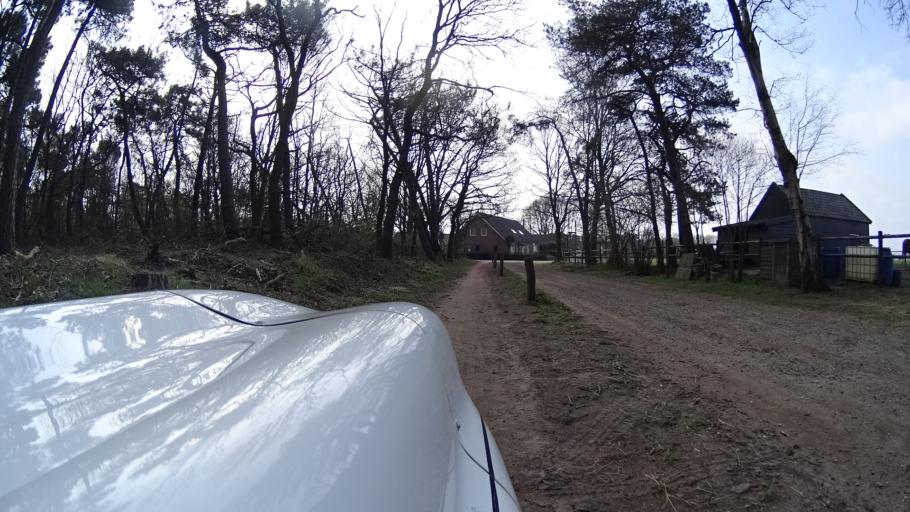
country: NL
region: North Brabant
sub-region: Gemeente Boekel
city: Boekel
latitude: 51.5792
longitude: 5.6983
